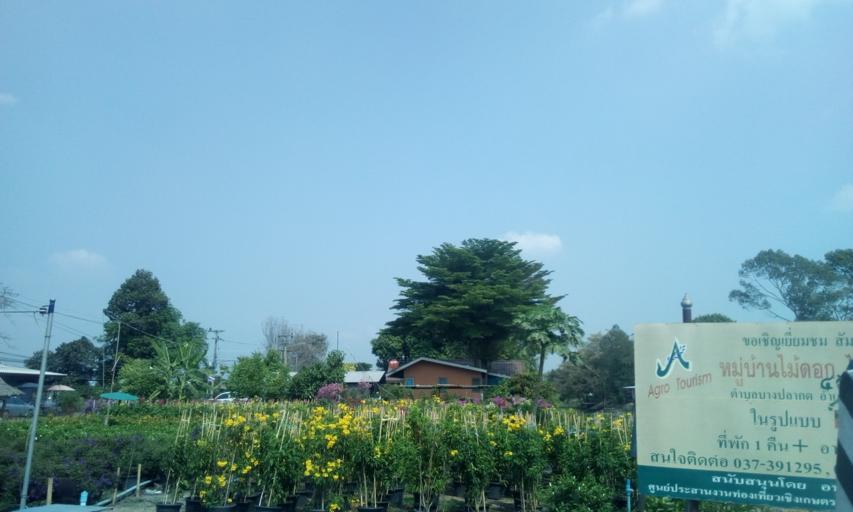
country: TH
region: Nakhon Nayok
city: Ongkharak
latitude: 14.1436
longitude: 100.9781
